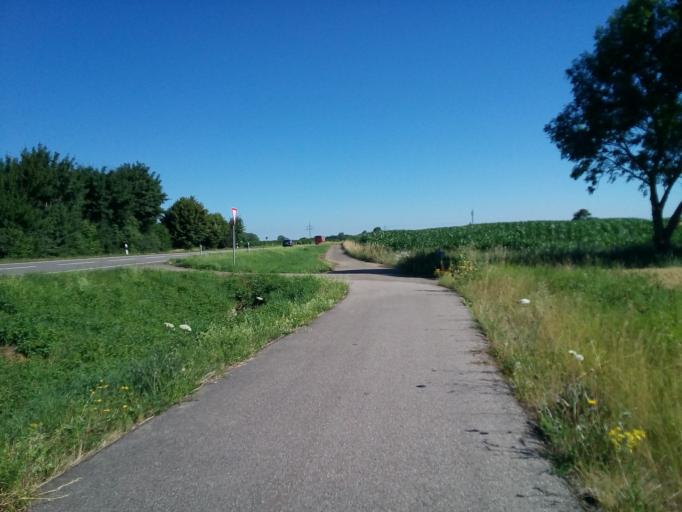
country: DE
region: Baden-Wuerttemberg
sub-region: Freiburg Region
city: Rheinau
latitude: 48.6885
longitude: 7.9753
